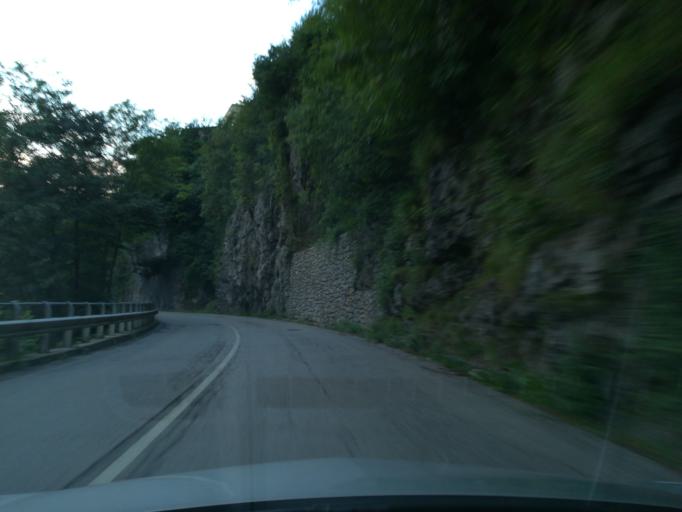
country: IT
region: Lombardy
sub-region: Provincia di Bergamo
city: Sant'Omobono Terme
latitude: 45.8043
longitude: 9.5418
